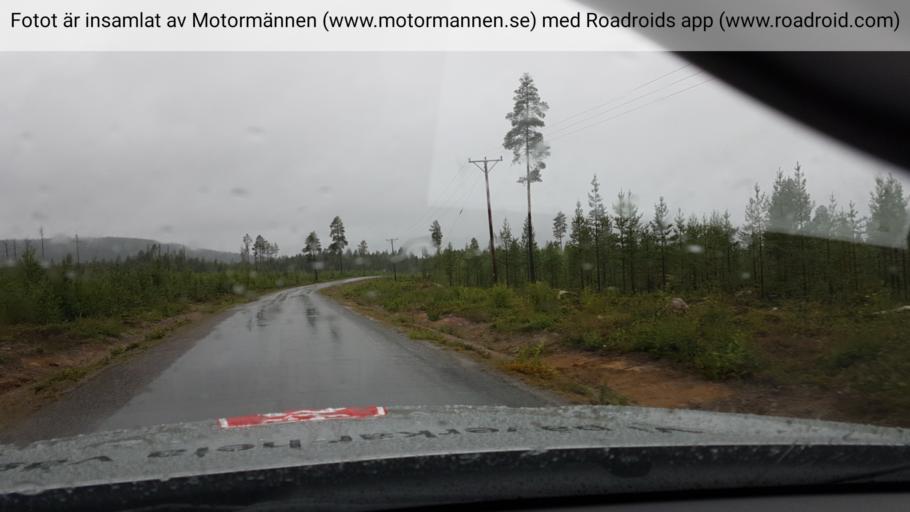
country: SE
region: Norrbotten
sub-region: Jokkmokks Kommun
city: Jokkmokk
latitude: 66.6002
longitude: 19.5240
